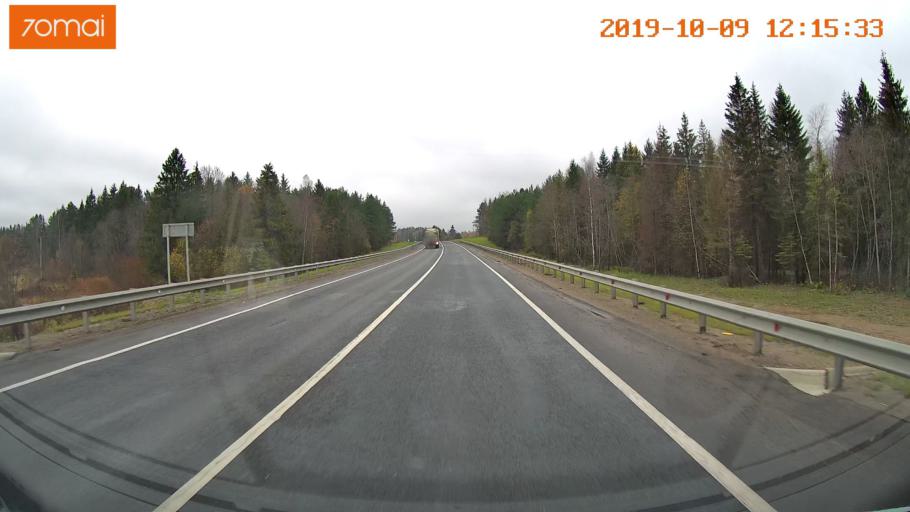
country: RU
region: Jaroslavl
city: Prechistoye
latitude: 58.4817
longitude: 40.3235
